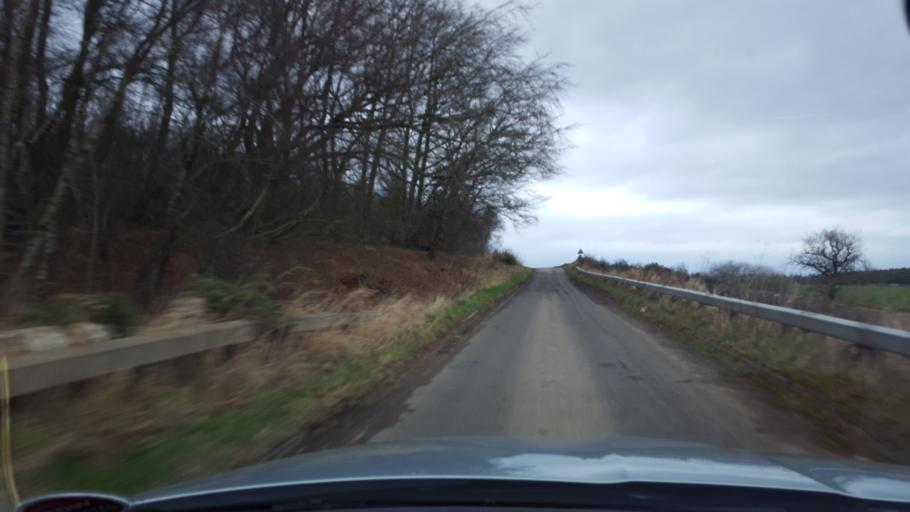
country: GB
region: Scotland
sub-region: West Lothian
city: Kirknewton
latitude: 55.8713
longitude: -3.4380
